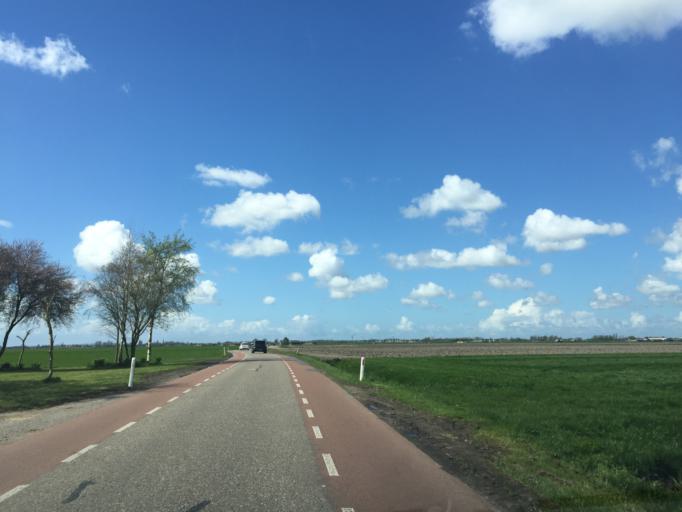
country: NL
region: South Holland
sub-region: Gemeente Kaag en Braassem
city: Leimuiden
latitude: 52.2044
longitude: 4.7104
